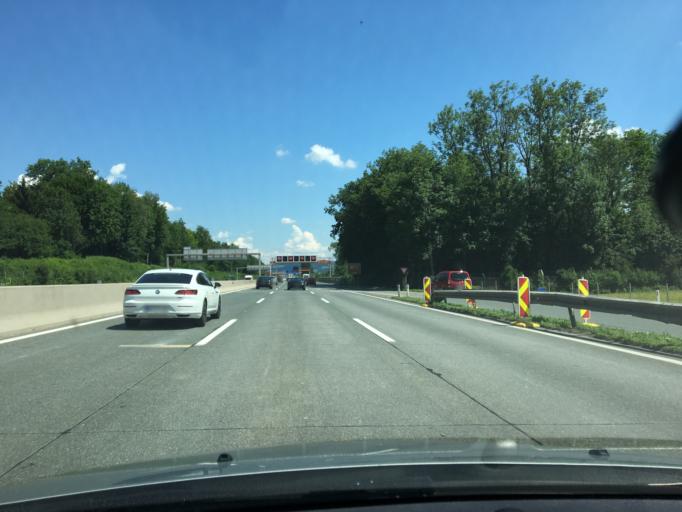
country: DE
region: Bavaria
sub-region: Upper Bavaria
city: Ainring
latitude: 47.7965
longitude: 12.9861
